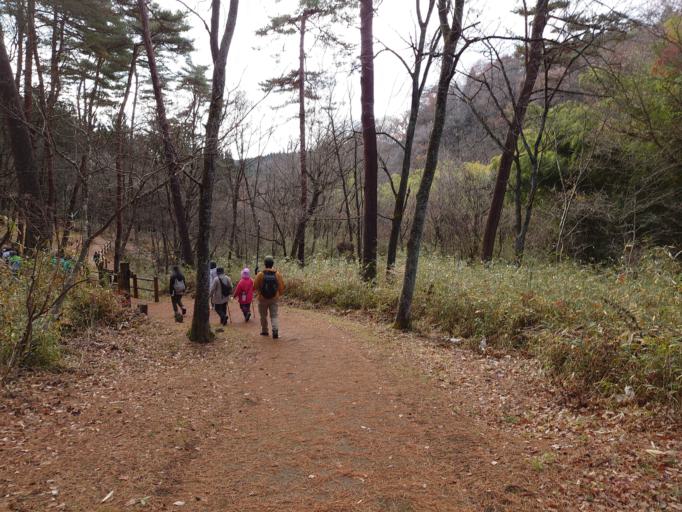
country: JP
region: Iwate
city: Ichinoseki
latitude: 38.9912
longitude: 141.1028
